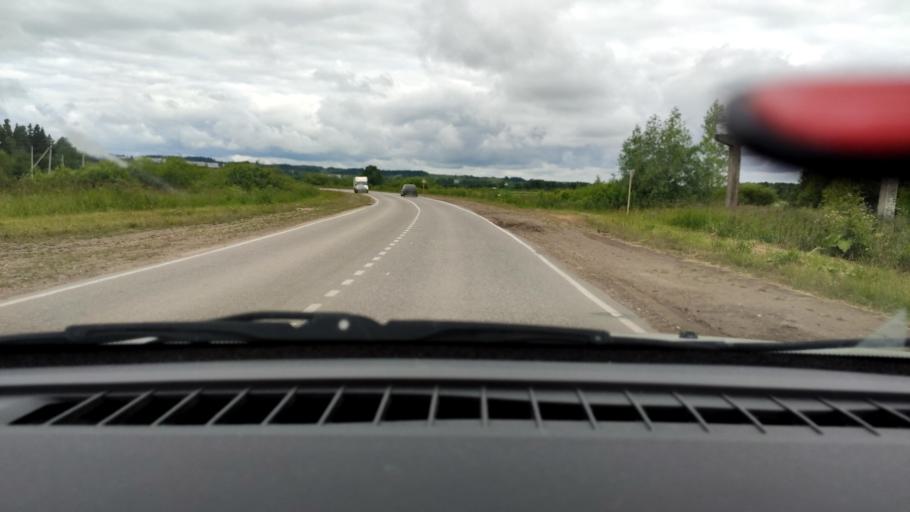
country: RU
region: Perm
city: Chaykovskaya
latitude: 58.0905
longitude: 55.6105
